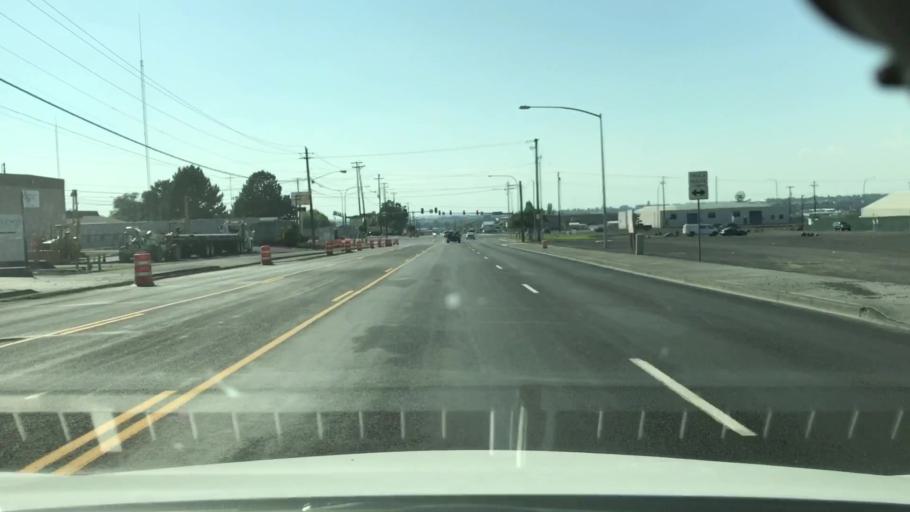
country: US
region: Washington
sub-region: Grant County
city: Moses Lake
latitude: 47.1311
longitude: -119.2541
